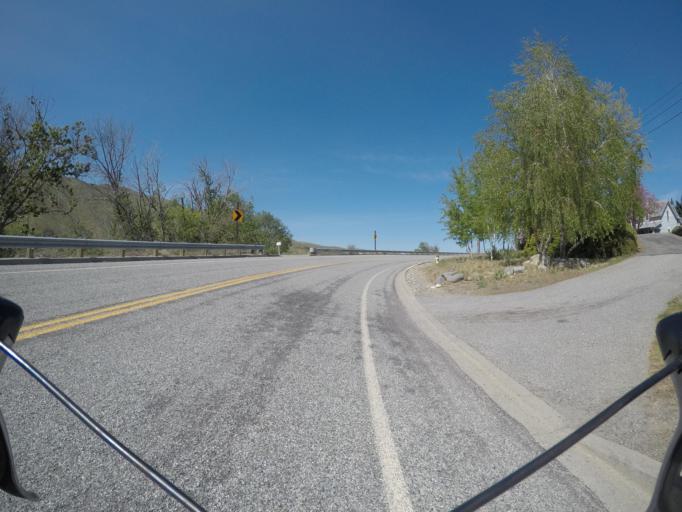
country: US
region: Washington
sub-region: Chelan County
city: West Wenatchee
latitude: 47.4705
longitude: -120.3669
